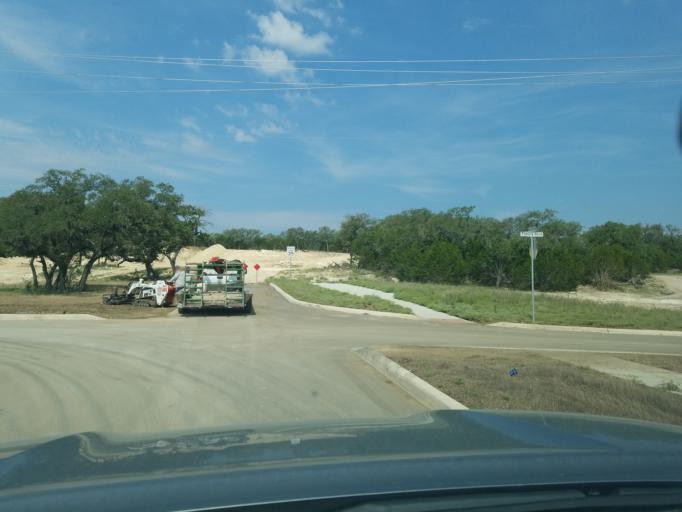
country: US
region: Texas
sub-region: Kendall County
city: Boerne
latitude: 29.7563
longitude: -98.7190
